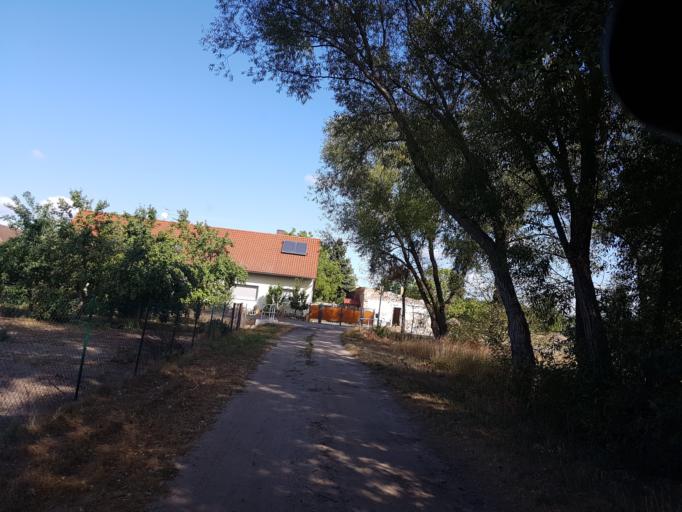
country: DE
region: Brandenburg
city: Sonnewalde
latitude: 51.6681
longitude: 13.6499
